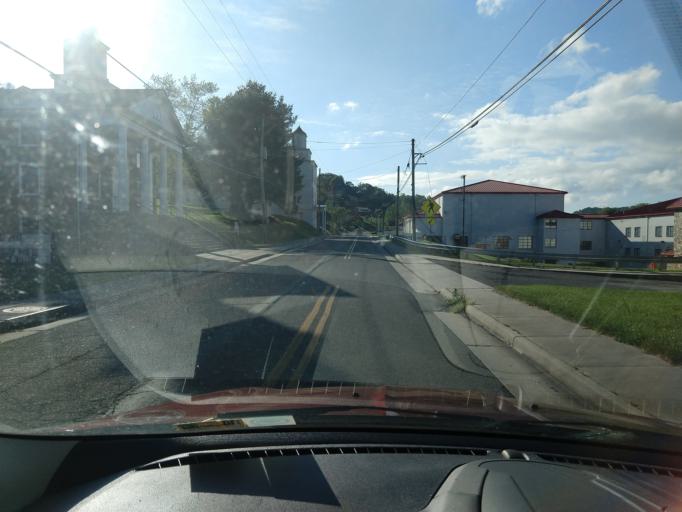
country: US
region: Virginia
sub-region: City of Galax
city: Galax
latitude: 36.7151
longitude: -80.9739
